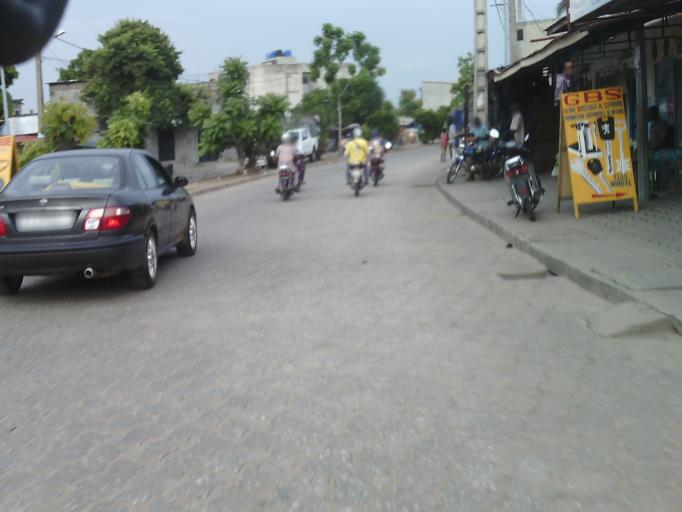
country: BJ
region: Littoral
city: Cotonou
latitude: 6.3919
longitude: 2.3685
